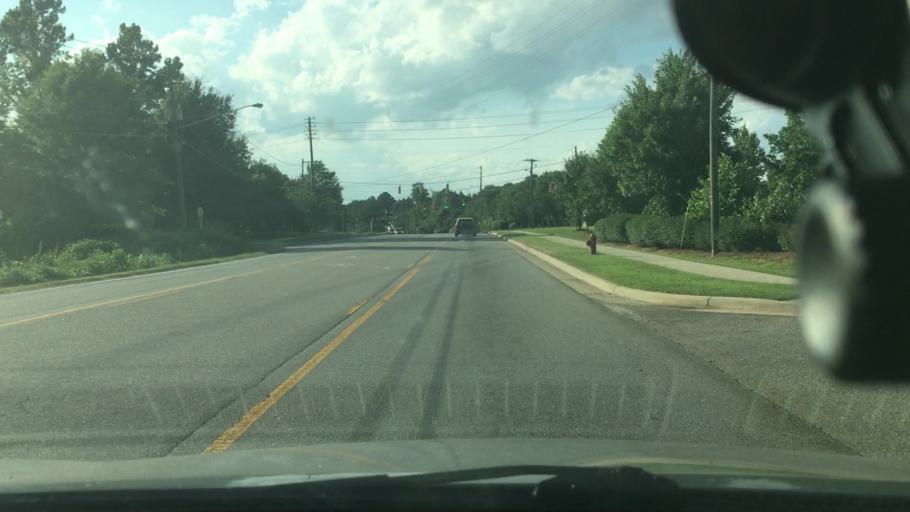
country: US
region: North Carolina
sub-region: Wake County
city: Apex
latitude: 35.7346
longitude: -78.8619
